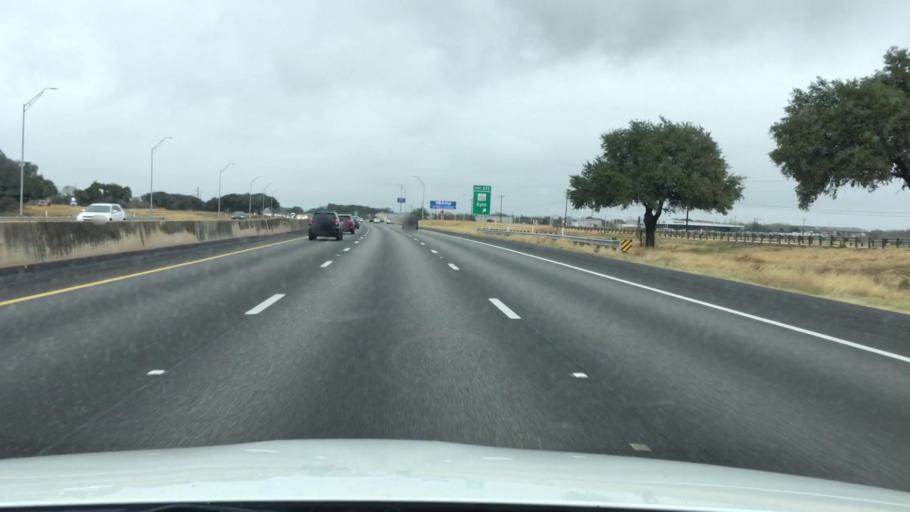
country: US
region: Texas
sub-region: Hays County
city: Kyle
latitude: 29.9479
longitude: -97.8793
